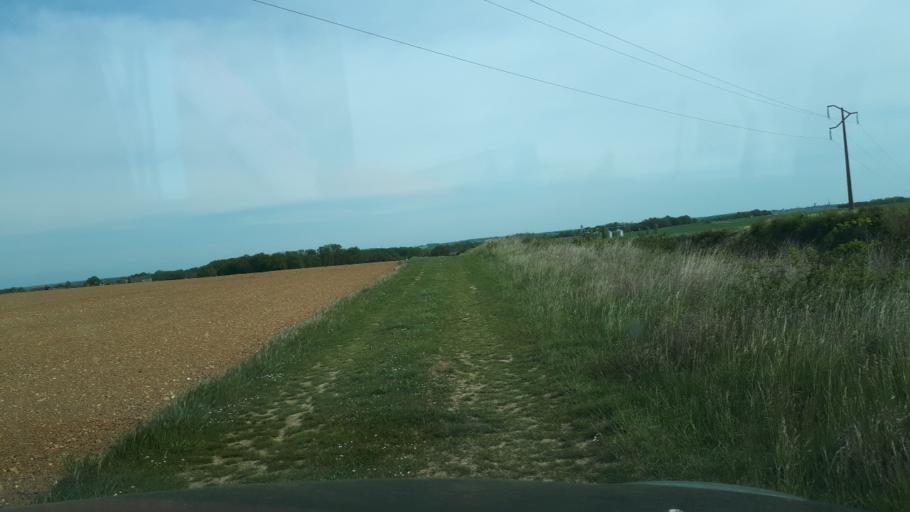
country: FR
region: Centre
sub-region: Departement du Loir-et-Cher
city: Naveil
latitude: 47.7649
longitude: 1.0173
